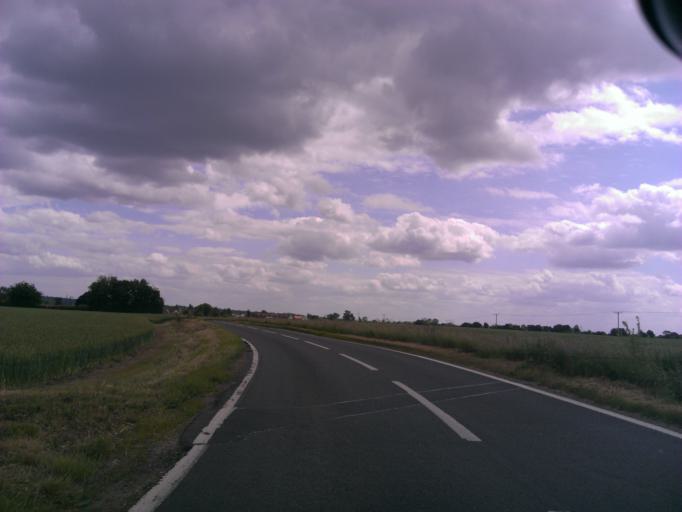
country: GB
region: England
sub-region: Essex
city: Witham
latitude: 51.8337
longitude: 0.6487
